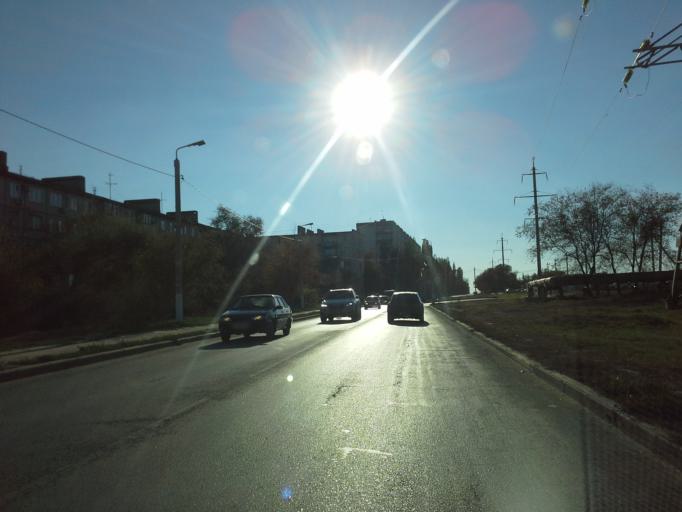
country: RU
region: Volgograd
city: Vodstroy
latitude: 48.8231
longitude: 44.6243
